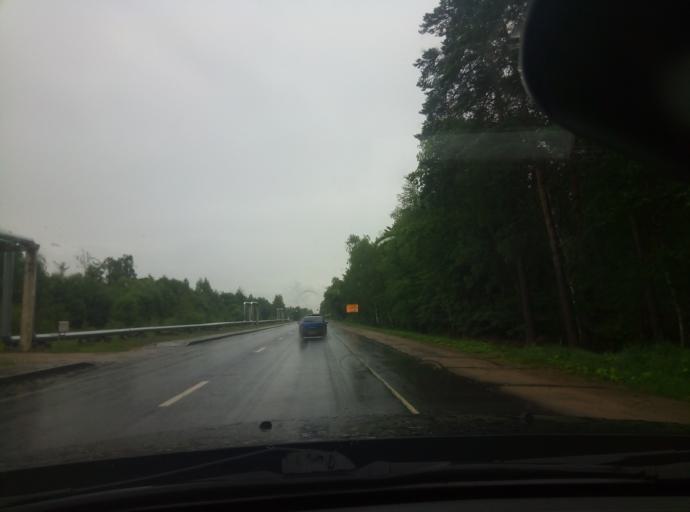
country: RU
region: Moskovskaya
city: Protvino
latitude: 54.8843
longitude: 37.2021
